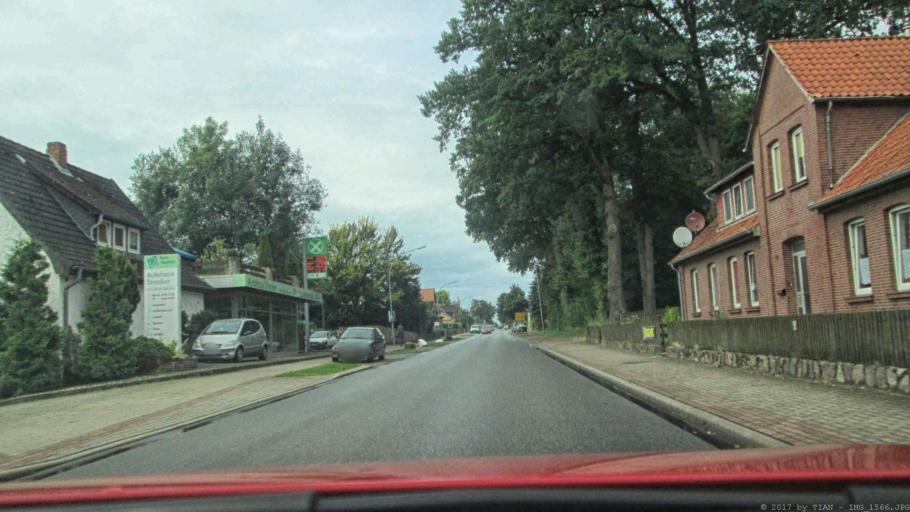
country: DE
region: Lower Saxony
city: Wieren
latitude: 52.8865
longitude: 10.6575
